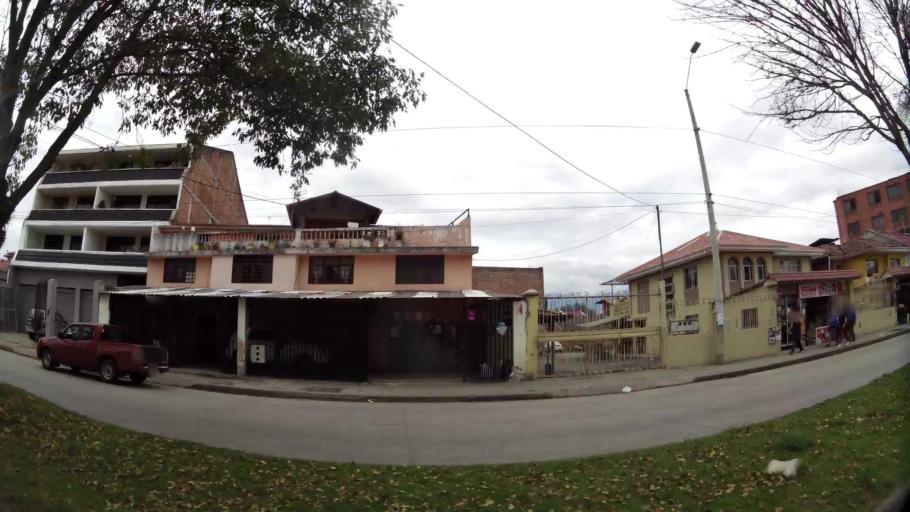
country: EC
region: Azuay
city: Cuenca
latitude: -2.9176
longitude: -79.0344
